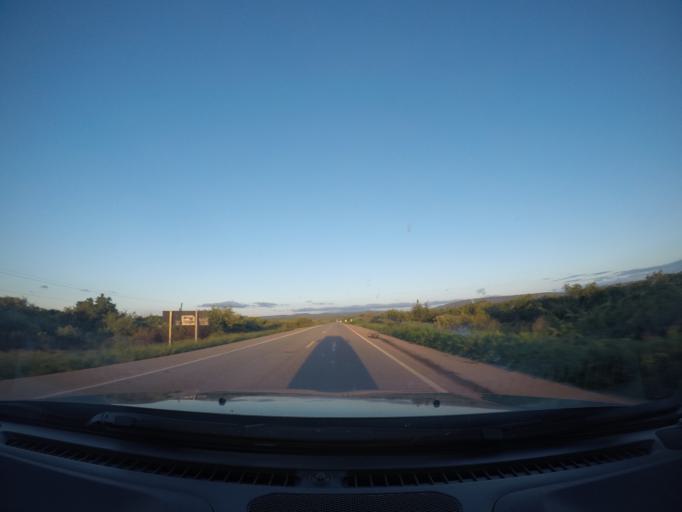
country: BR
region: Bahia
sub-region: Seabra
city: Seabra
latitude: -12.3999
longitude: -41.9423
